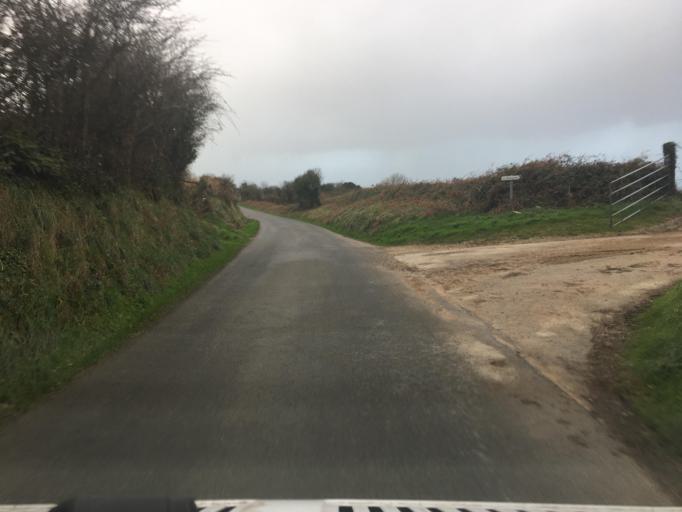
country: FR
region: Lower Normandy
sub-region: Departement de la Manche
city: Beaumont-Hague
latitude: 49.6857
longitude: -1.8693
